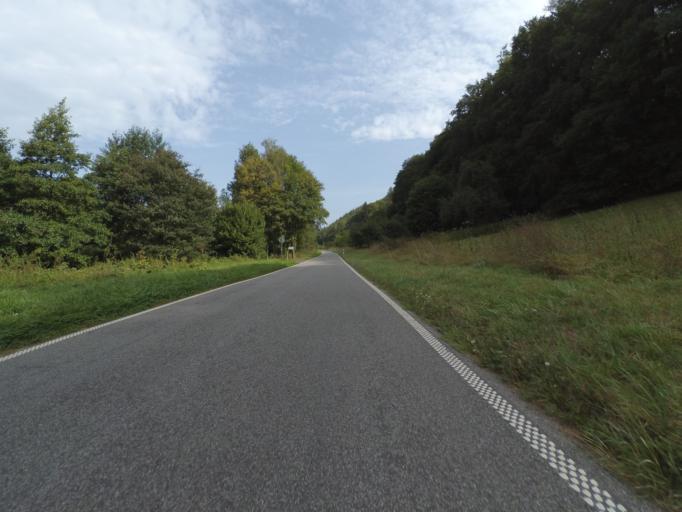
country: DE
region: Rheinland-Pfalz
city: Tawern
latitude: 49.6630
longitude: 6.5140
